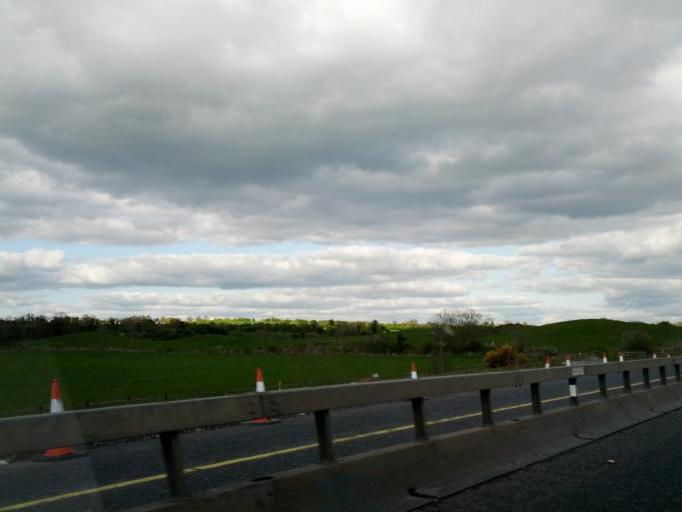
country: IE
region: Leinster
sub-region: An Iarmhi
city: Athlone
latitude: 53.4005
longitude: -7.8366
